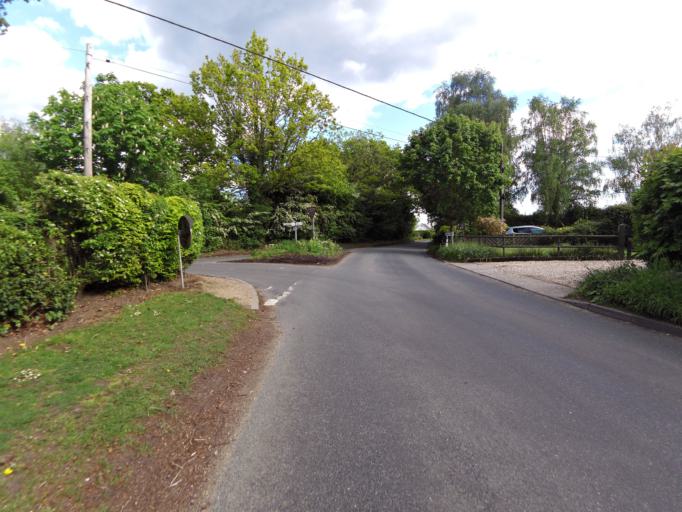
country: GB
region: England
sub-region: Suffolk
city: Elmswell
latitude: 52.2112
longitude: 0.9161
